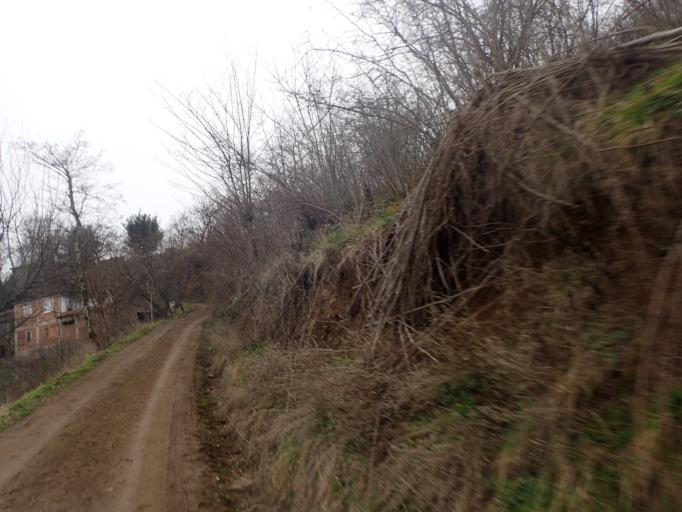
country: TR
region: Ordu
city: Camas
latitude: 40.9180
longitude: 37.5671
